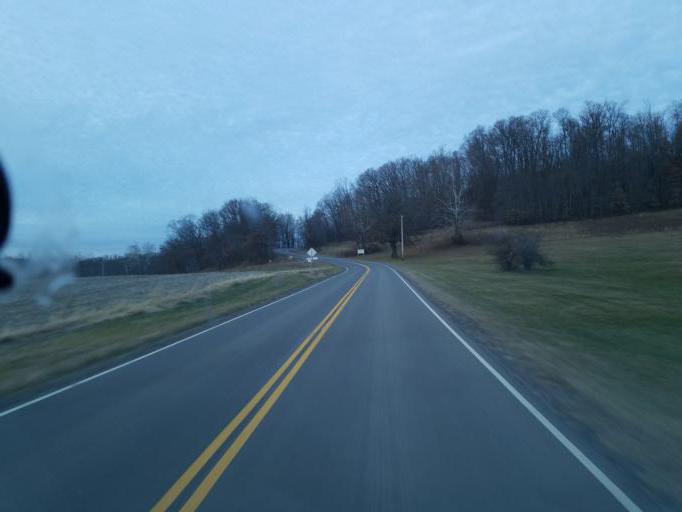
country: US
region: Ohio
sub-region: Muskingum County
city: Dresden
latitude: 40.1696
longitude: -82.0272
